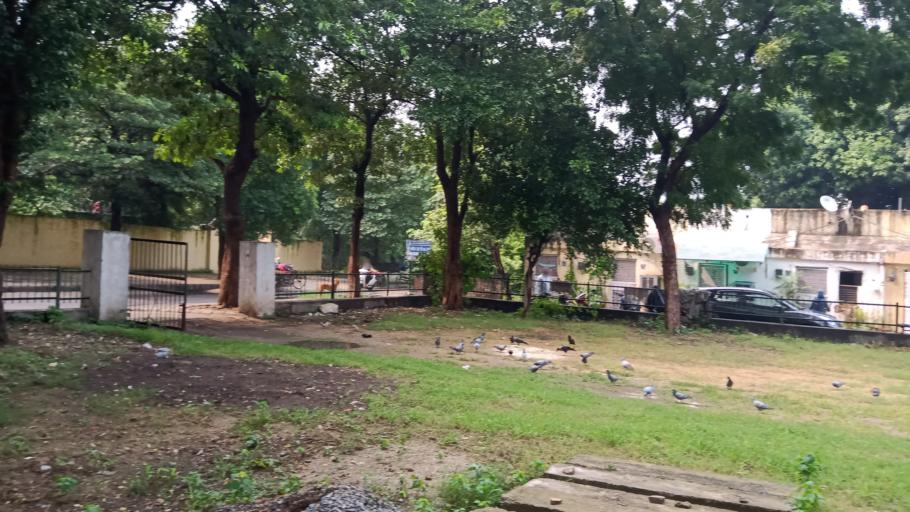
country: IN
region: NCT
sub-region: New Delhi
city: New Delhi
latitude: 28.5767
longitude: 77.2480
